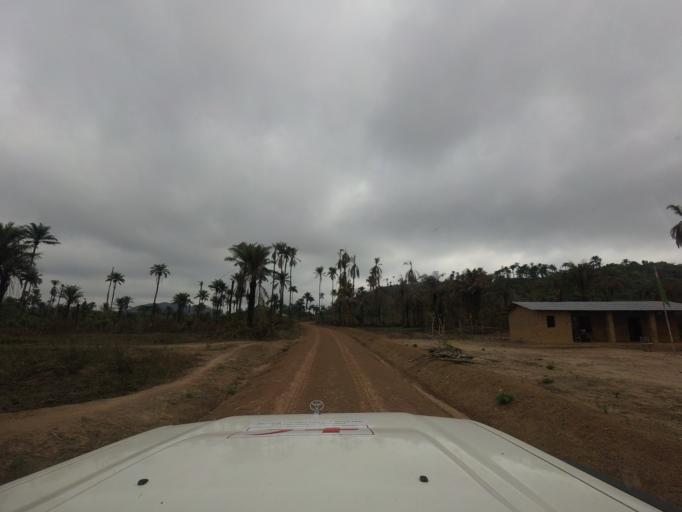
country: LR
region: Lofa
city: Voinjama
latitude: 8.4426
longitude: -9.7946
